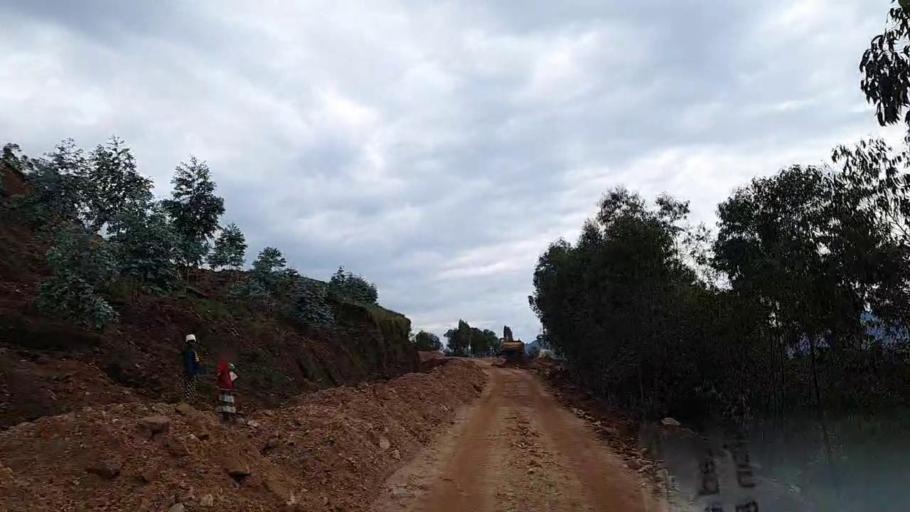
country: RW
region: Southern Province
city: Nzega
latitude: -2.3723
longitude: 29.4492
